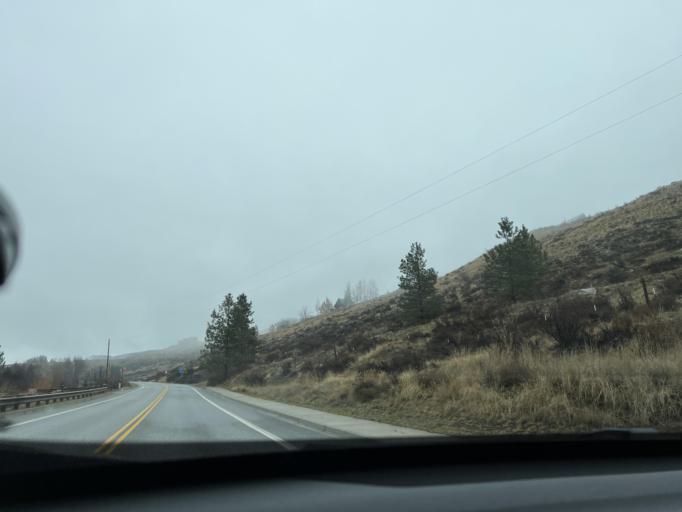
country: US
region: Washington
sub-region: Okanogan County
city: Brewster
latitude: 48.4825
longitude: -120.1786
